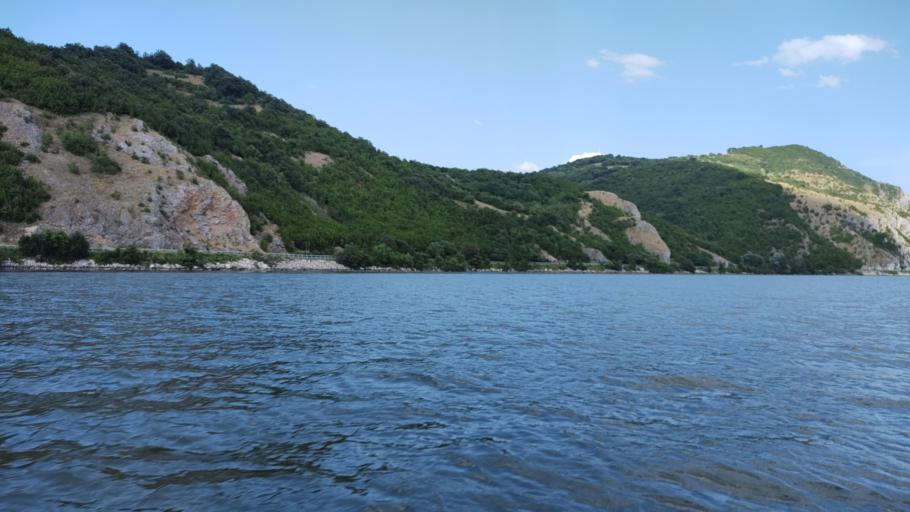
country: RO
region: Caras-Severin
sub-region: Comuna Pescari
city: Coronini
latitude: 44.6686
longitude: 21.6836
